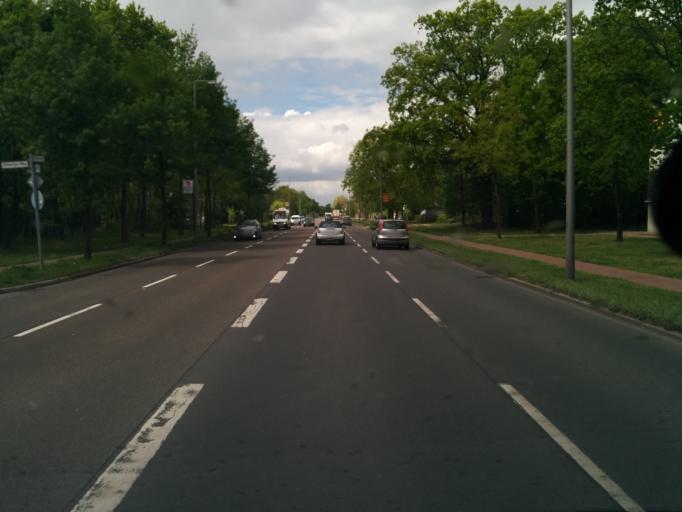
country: DE
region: Berlin
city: Staaken
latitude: 52.5272
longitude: 13.1293
